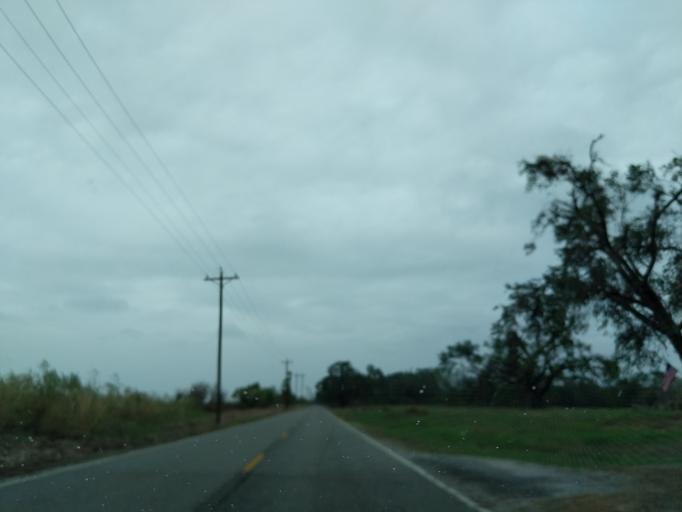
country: US
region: Louisiana
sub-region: Jefferson Davis Parish
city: Lake Arthur
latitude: 29.7538
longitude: -92.9160
